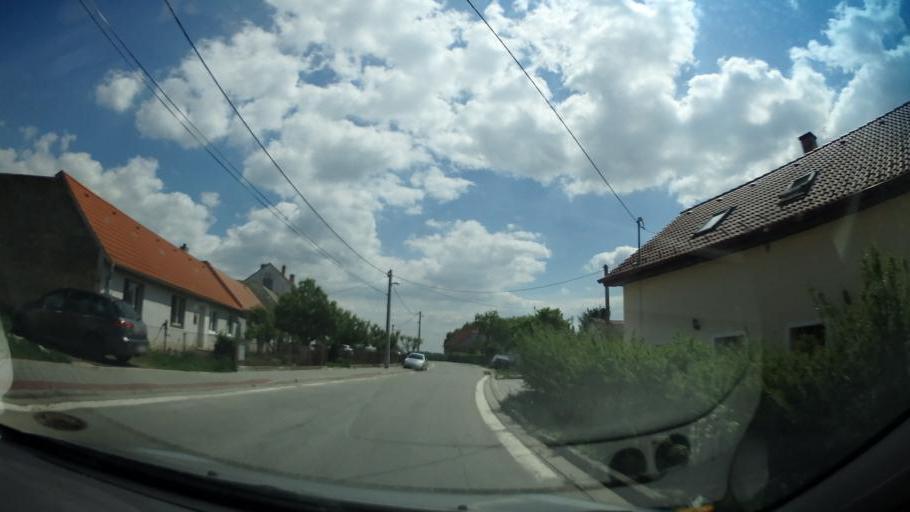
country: CZ
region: Vysocina
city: Hrotovice
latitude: 49.1287
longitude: 16.0837
